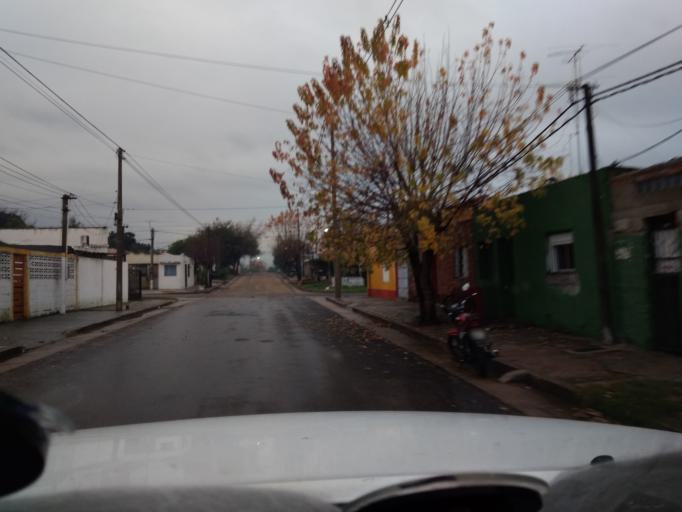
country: UY
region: Florida
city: Florida
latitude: -34.1064
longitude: -56.2149
